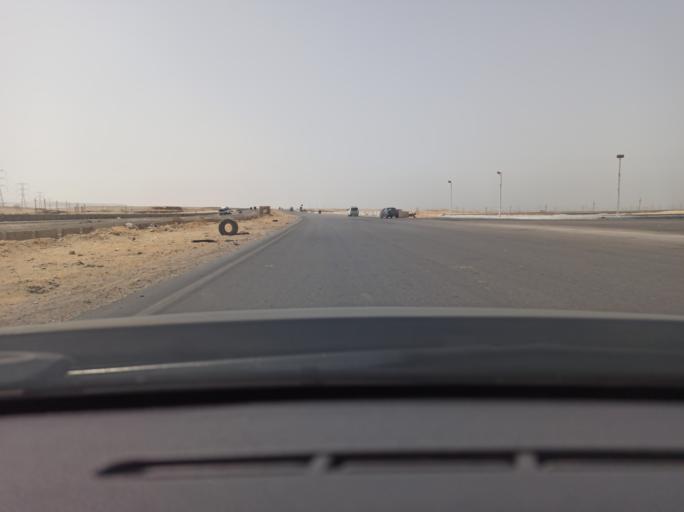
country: EG
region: Muhafazat al Fayyum
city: Al Wasitah
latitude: 29.3824
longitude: 31.3142
